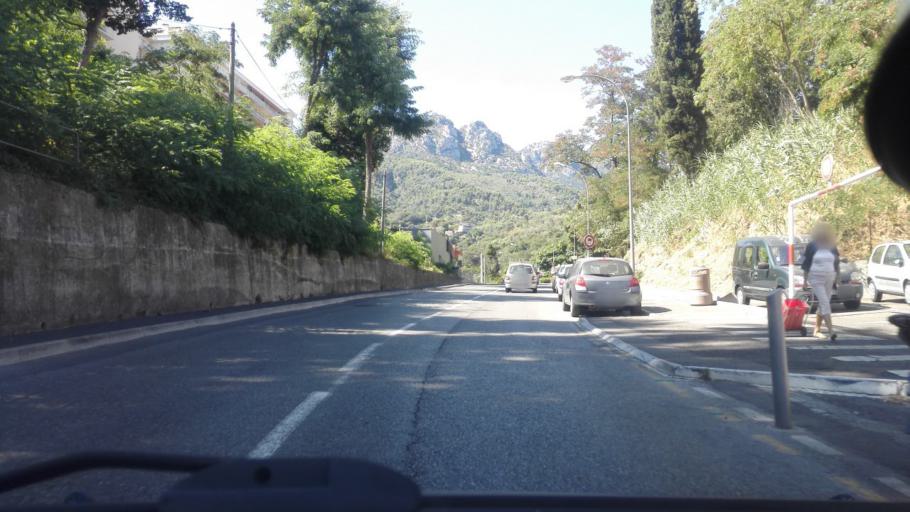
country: FR
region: Provence-Alpes-Cote d'Azur
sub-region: Departement des Alpes-Maritimes
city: Roquebrune-Cap-Martin
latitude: 43.7807
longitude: 7.4809
